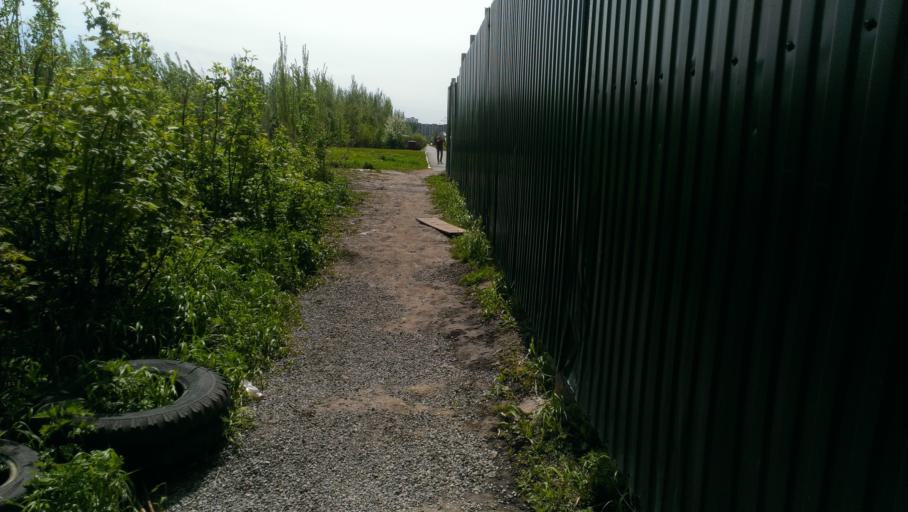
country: RU
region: Altai Krai
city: Novosilikatnyy
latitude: 53.3563
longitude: 83.6576
